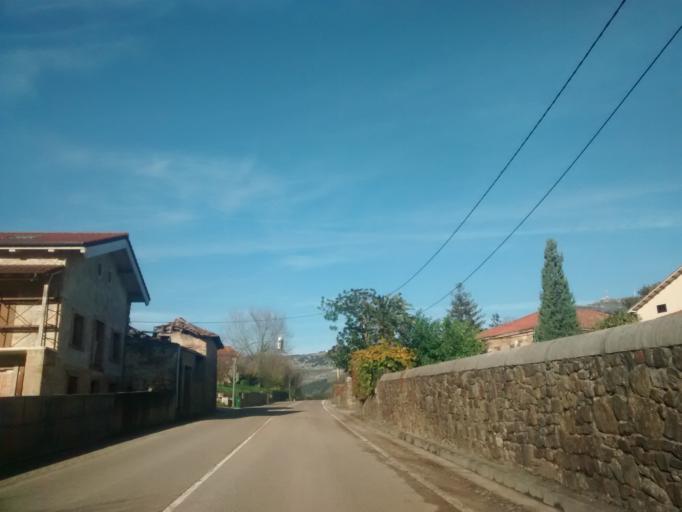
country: ES
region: Cantabria
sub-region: Provincia de Cantabria
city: Lierganes
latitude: 43.3544
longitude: -3.7636
